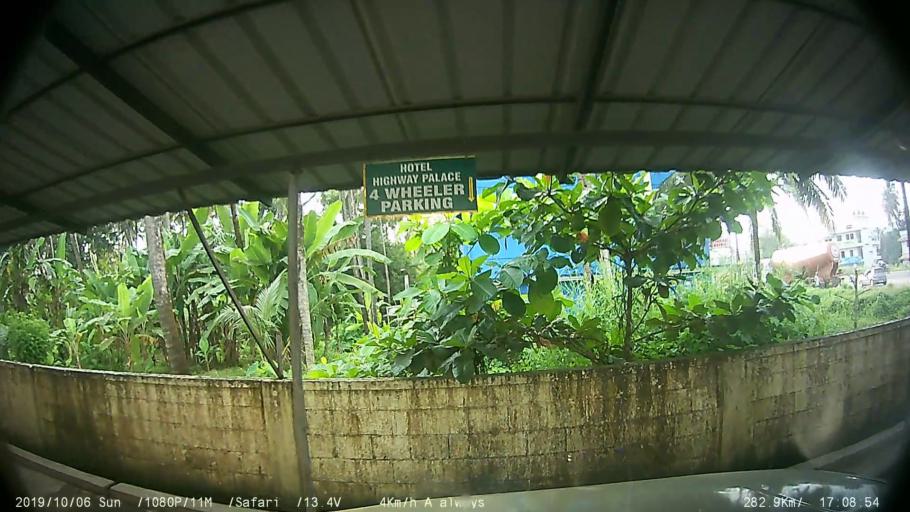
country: IN
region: Kerala
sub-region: Thrissur District
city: Trichur
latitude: 10.5561
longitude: 76.3225
